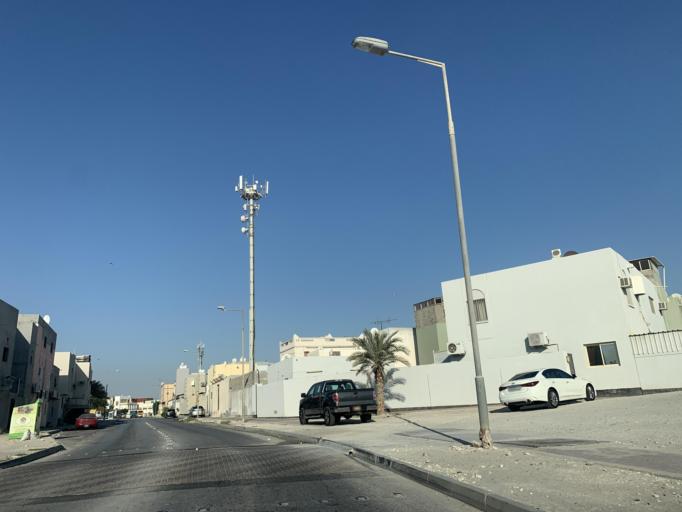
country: BH
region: Central Governorate
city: Madinat Hamad
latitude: 26.1111
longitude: 50.5066
